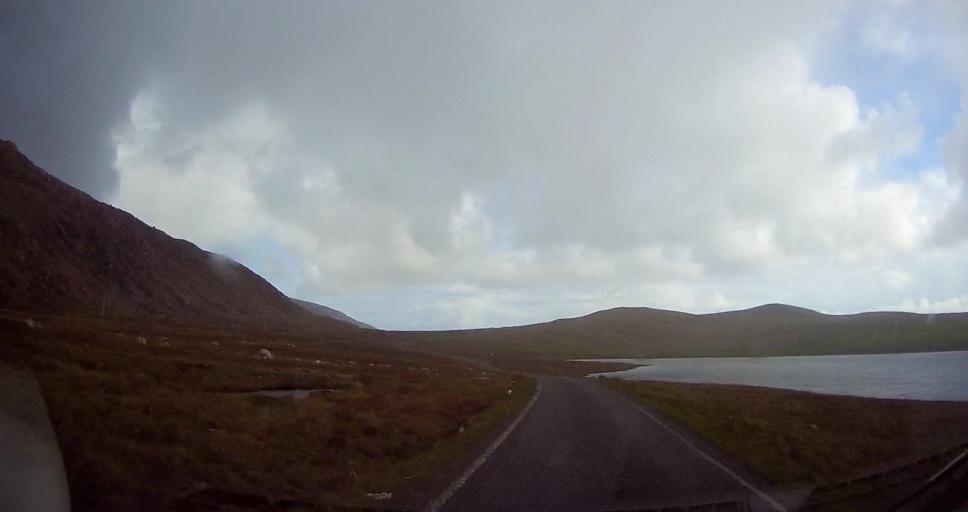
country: GB
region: Scotland
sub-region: Shetland Islands
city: Lerwick
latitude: 60.5486
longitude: -1.3408
